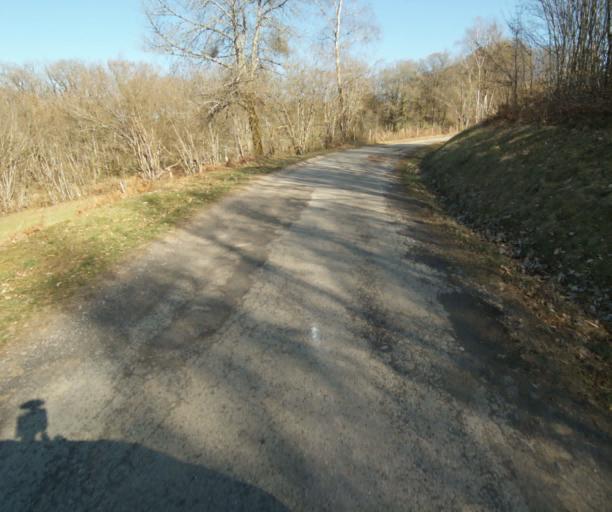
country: FR
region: Limousin
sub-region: Departement de la Correze
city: Chamboulive
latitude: 45.4869
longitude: 1.6928
